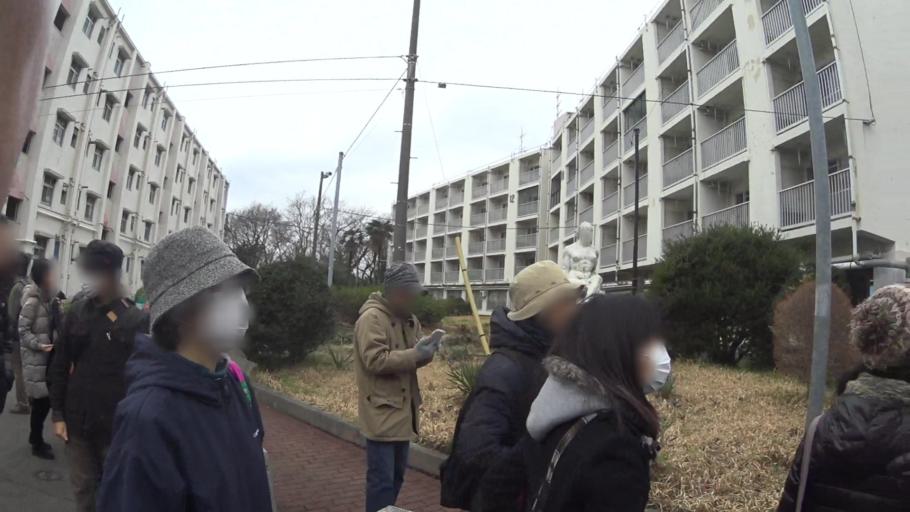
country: JP
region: Tokyo
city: Chofugaoka
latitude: 35.6338
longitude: 139.6098
